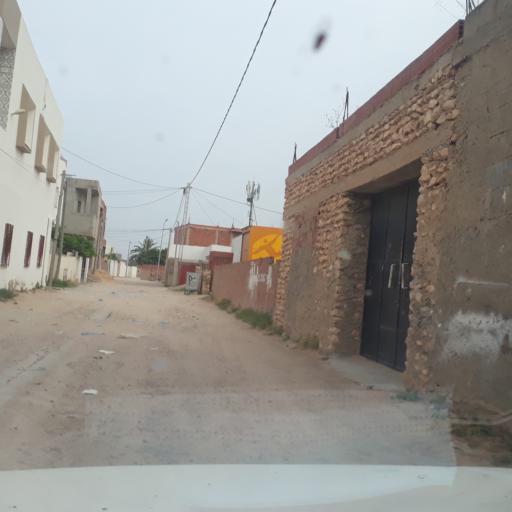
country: TN
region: Safaqis
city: Al Qarmadah
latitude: 34.8251
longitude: 10.7780
